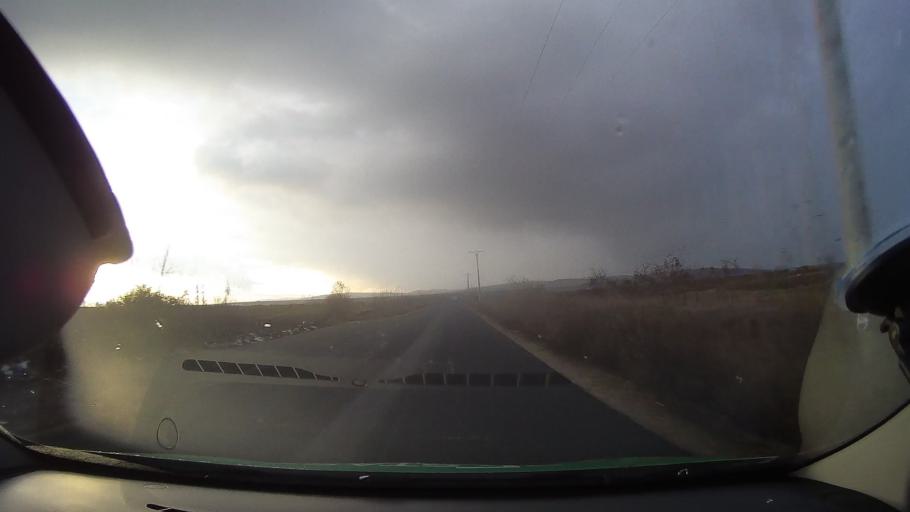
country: RO
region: Cluj
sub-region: Comuna Luna
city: Luncani
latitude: 46.4490
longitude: 23.9367
